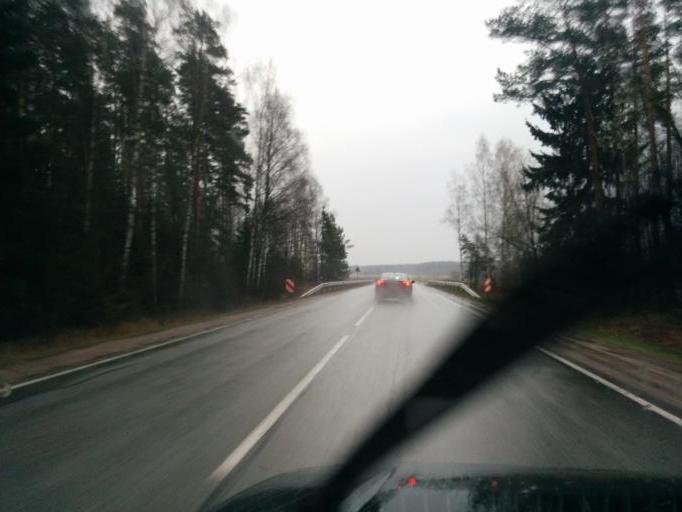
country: LV
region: Kekava
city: Kekava
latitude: 56.8116
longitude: 24.1621
